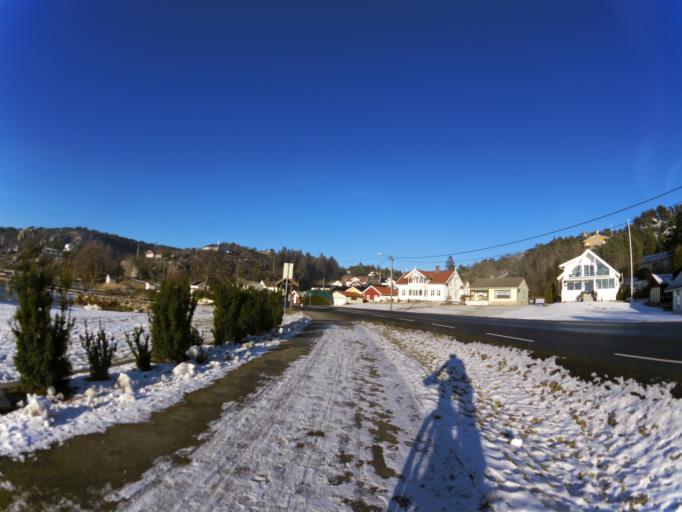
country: NO
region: Ostfold
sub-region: Fredrikstad
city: Lervik
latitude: 59.2062
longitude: 10.8061
